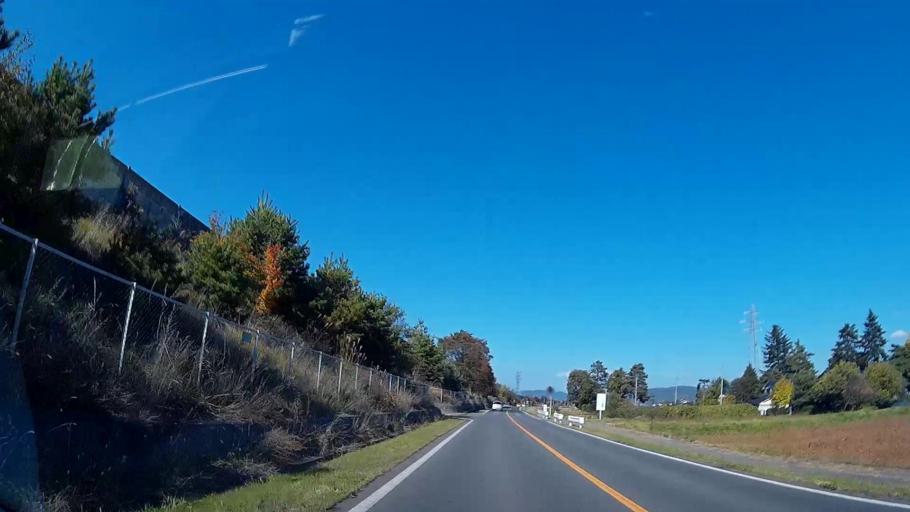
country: JP
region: Nagano
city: Matsumoto
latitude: 36.2093
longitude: 137.9299
